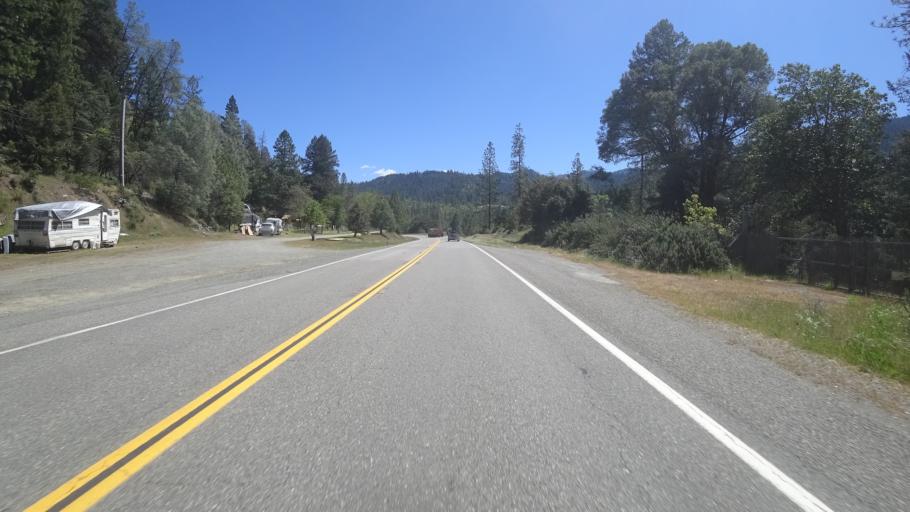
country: US
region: California
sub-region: Trinity County
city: Hayfork
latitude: 40.7433
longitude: -123.2675
